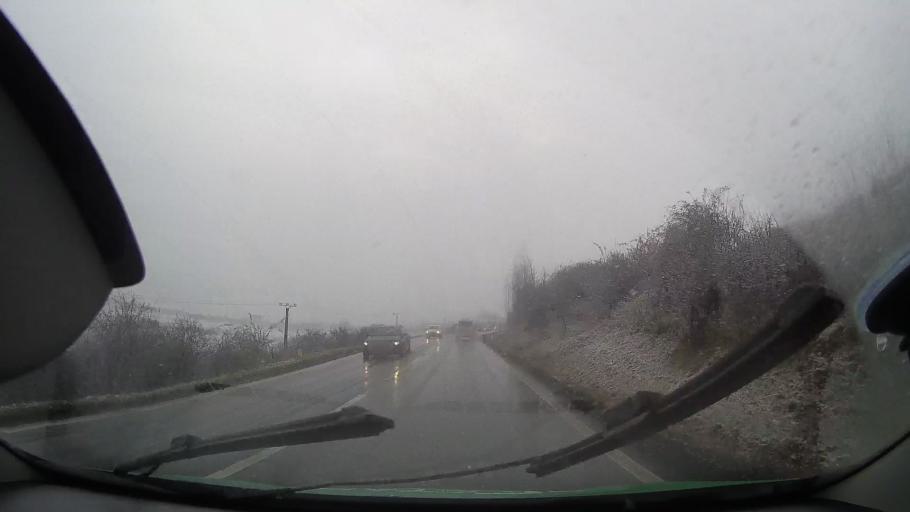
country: RO
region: Mures
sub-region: Comuna Bagaciu
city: Delenii
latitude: 46.2608
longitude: 24.3013
